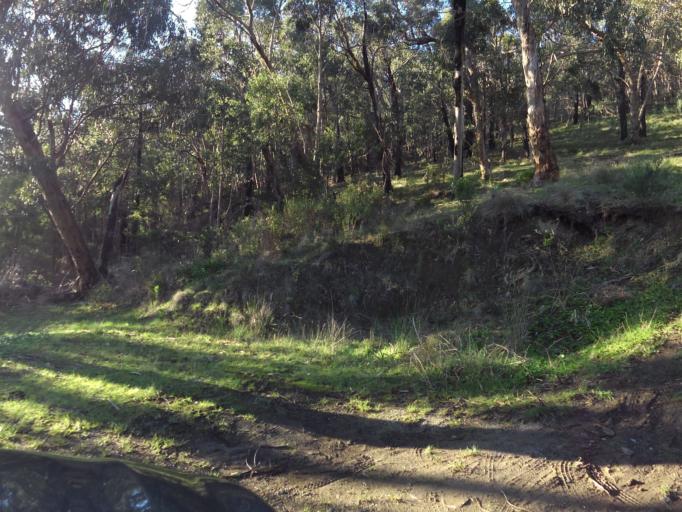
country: AU
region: Victoria
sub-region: Knox
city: Ferntree Gully
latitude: -37.8883
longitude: 145.3080
